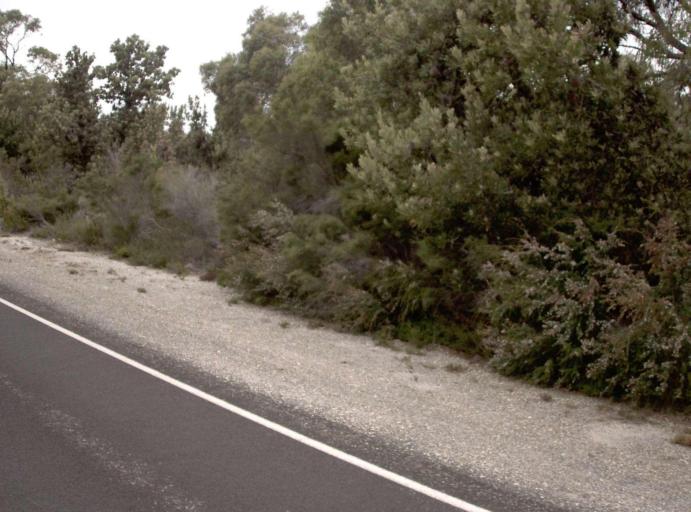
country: AU
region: Victoria
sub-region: Wellington
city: Sale
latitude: -38.1859
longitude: 147.3714
